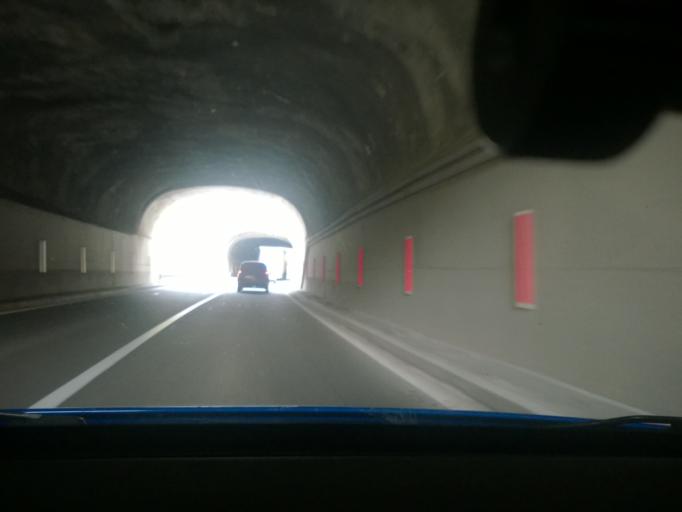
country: RS
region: Central Serbia
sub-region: Nisavski Okrug
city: Svrljig
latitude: 43.3274
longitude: 22.1611
